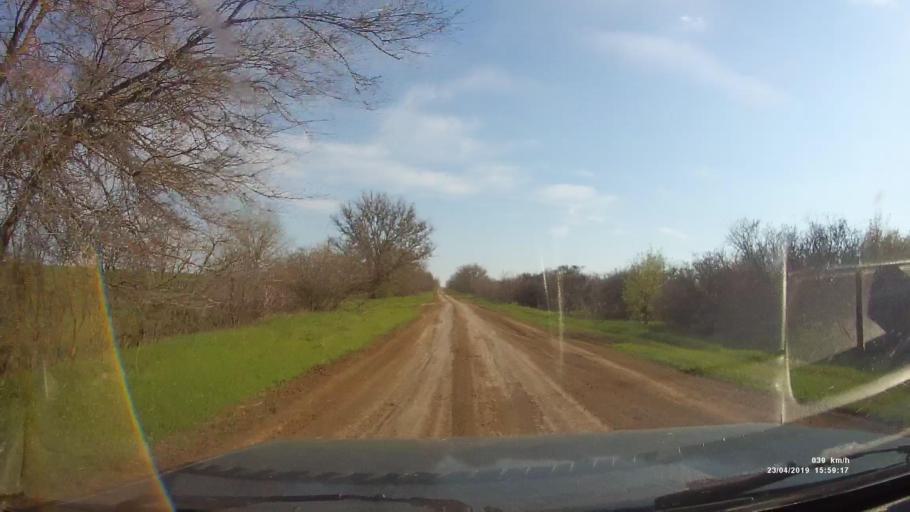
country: RU
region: Rostov
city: Remontnoye
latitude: 46.5179
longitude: 43.1096
